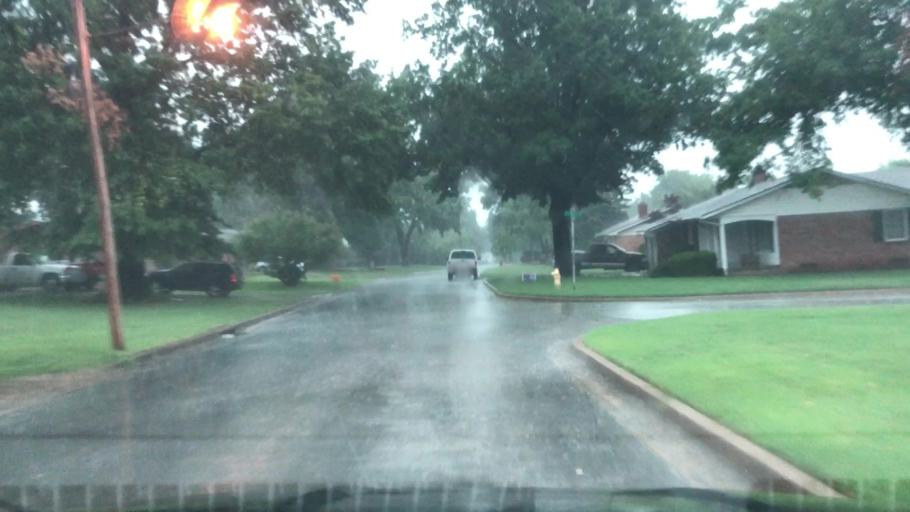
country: US
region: Oklahoma
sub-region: Tulsa County
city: Tulsa
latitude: 36.1352
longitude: -95.9174
